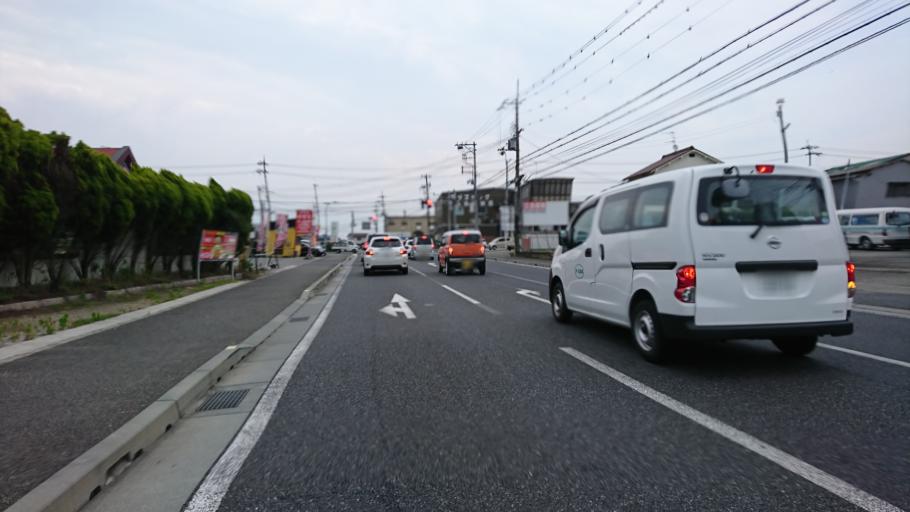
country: JP
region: Hyogo
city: Miki
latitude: 34.7322
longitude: 134.9216
